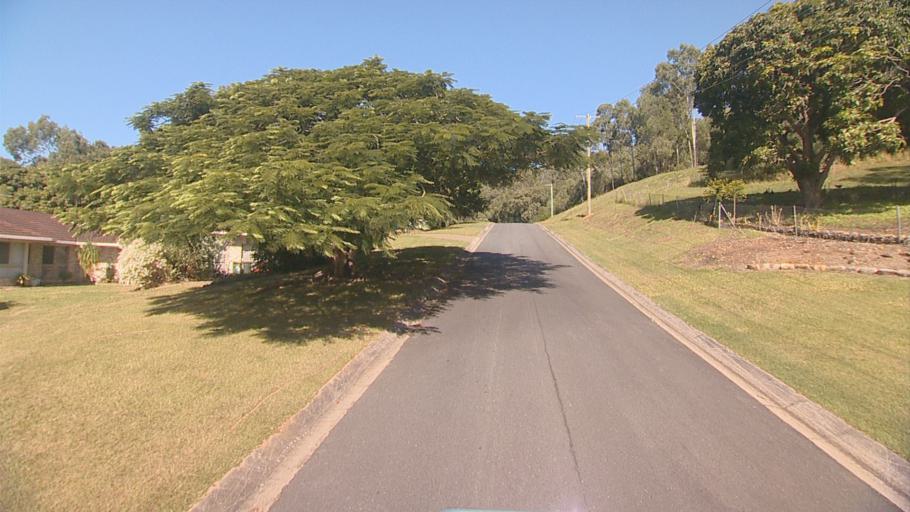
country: AU
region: Queensland
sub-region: Logan
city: Windaroo
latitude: -27.7436
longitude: 153.1834
